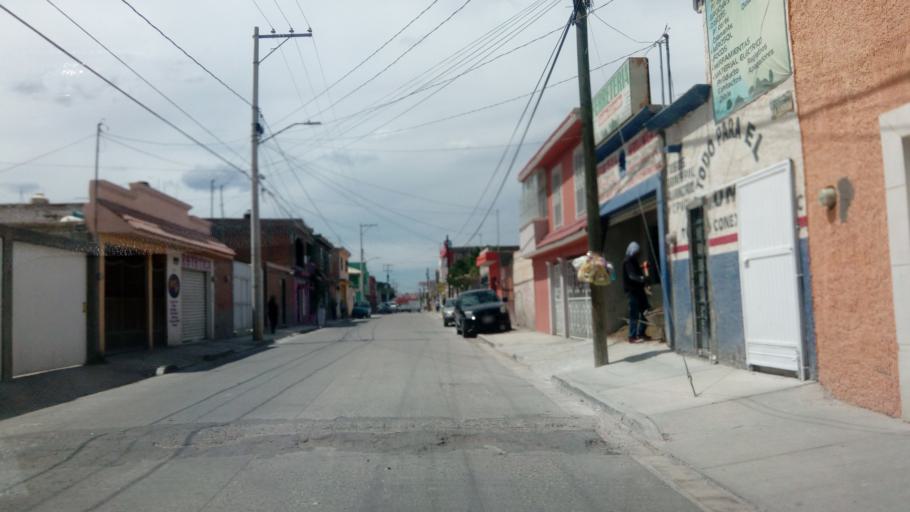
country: MX
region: Durango
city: Victoria de Durango
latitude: 23.9925
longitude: -104.6459
